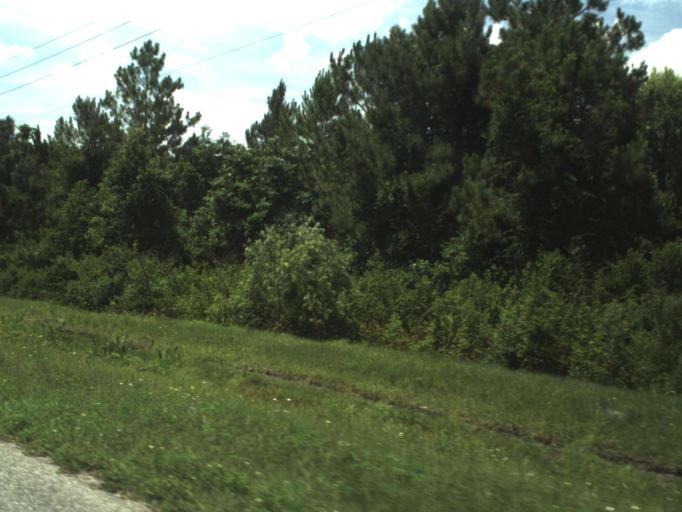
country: US
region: Florida
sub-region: Volusia County
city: Samsula-Spruce Creek
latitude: 29.0142
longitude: -81.0904
